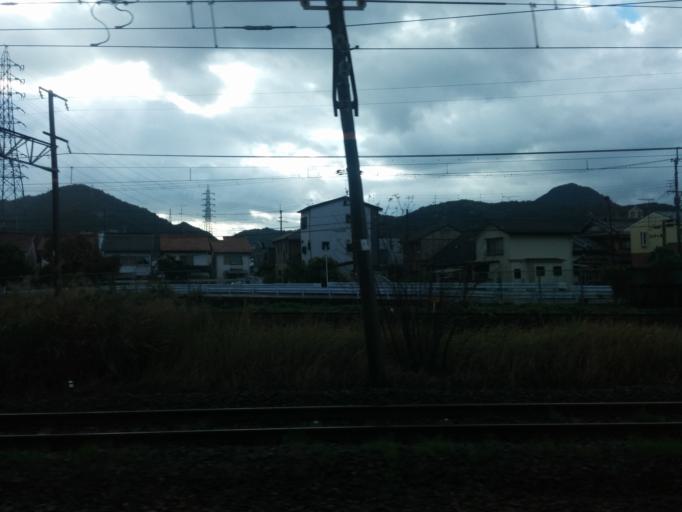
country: JP
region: Shiga Prefecture
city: Moriyama
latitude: 35.0731
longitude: 136.0290
